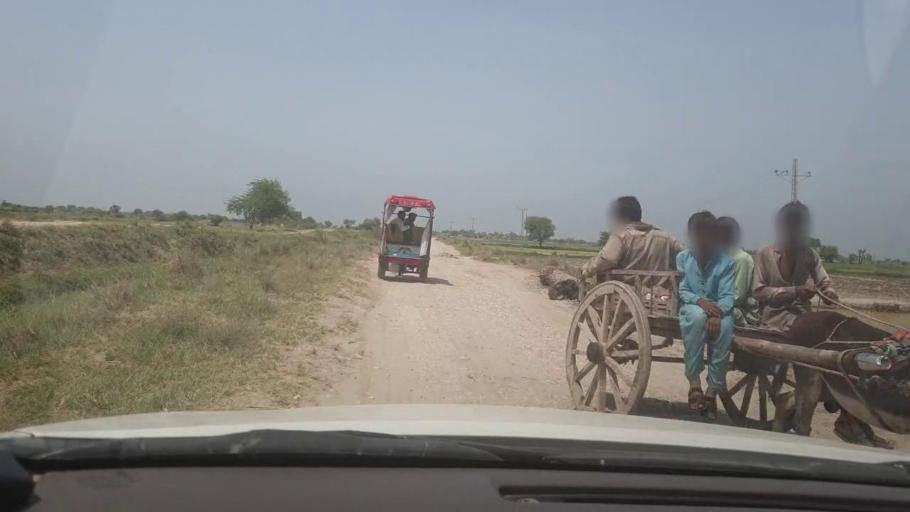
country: PK
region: Sindh
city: Shikarpur
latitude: 27.9369
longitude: 68.5755
